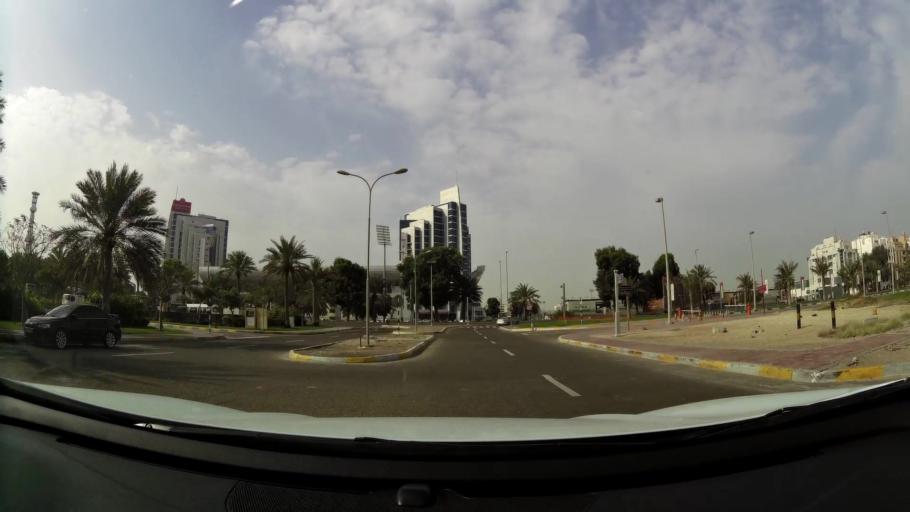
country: AE
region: Abu Dhabi
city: Abu Dhabi
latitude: 24.4554
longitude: 54.3941
